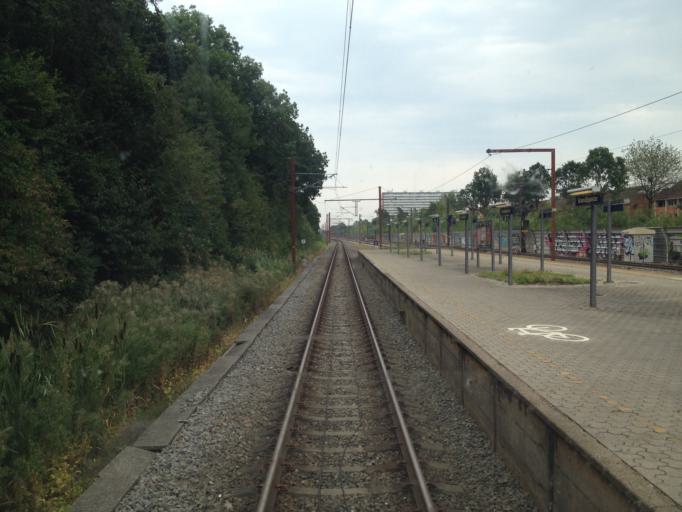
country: DK
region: Capital Region
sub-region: Rodovre Kommune
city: Rodovre
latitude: 55.6651
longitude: 12.4427
